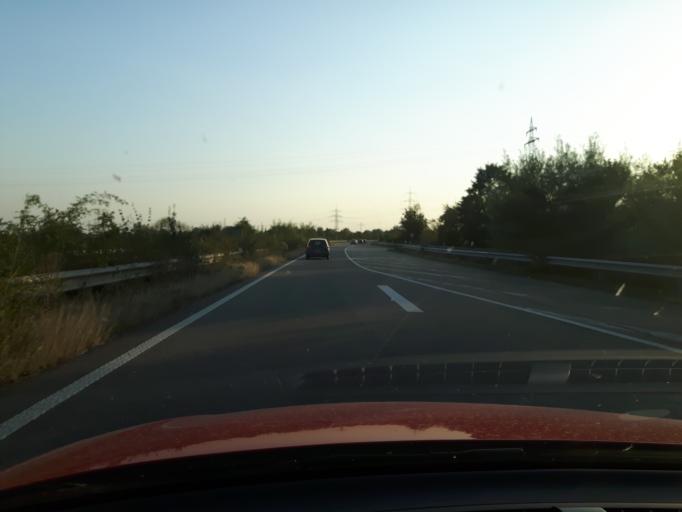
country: DE
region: Rheinland-Pfalz
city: Worth am Rhein
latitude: 49.0385
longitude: 8.2726
